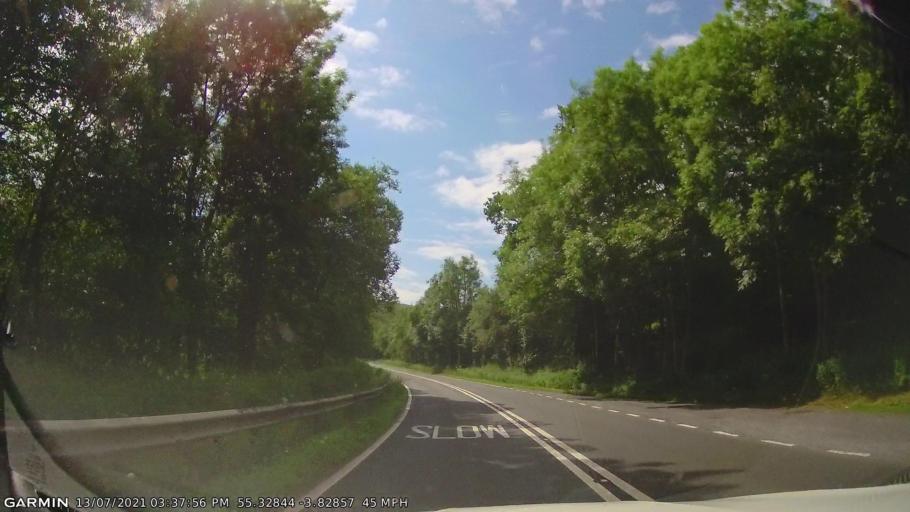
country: GB
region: Scotland
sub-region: Dumfries and Galloway
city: Sanquhar
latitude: 55.3284
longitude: -3.8286
